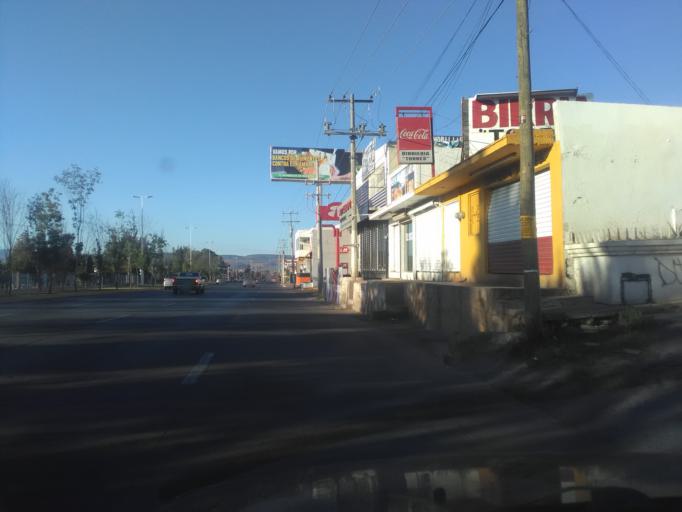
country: MX
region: Durango
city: Victoria de Durango
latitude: 24.0152
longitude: -104.6905
